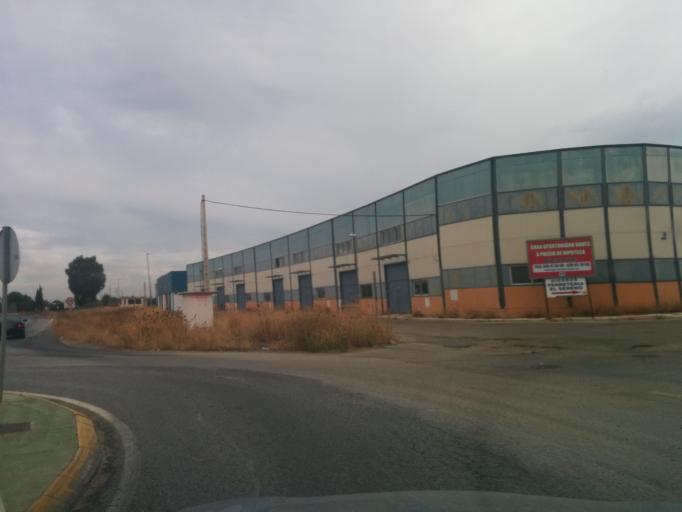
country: ES
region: Andalusia
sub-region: Provincia de Sevilla
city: La Rinconada
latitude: 37.4988
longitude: -6.0121
